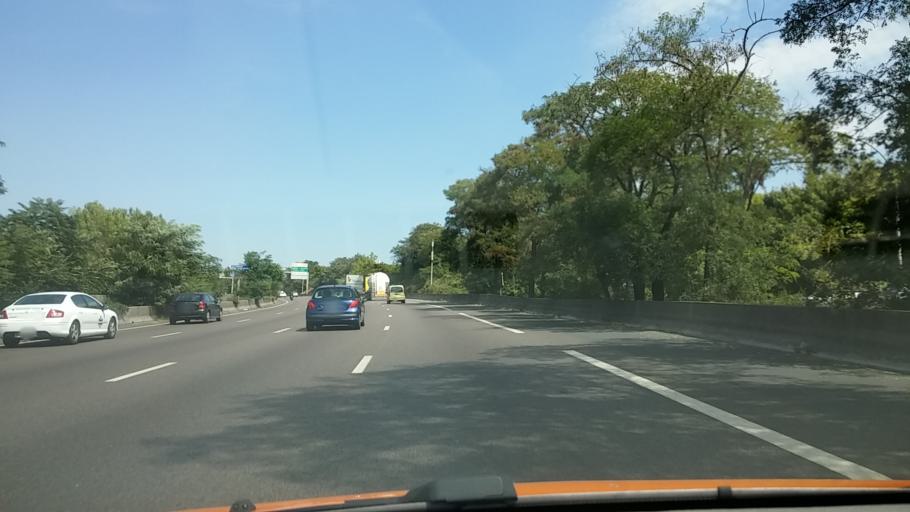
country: FR
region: Ile-de-France
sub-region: Departement du Val-de-Marne
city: Bry-sur-Marne
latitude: 48.8269
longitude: 2.5241
